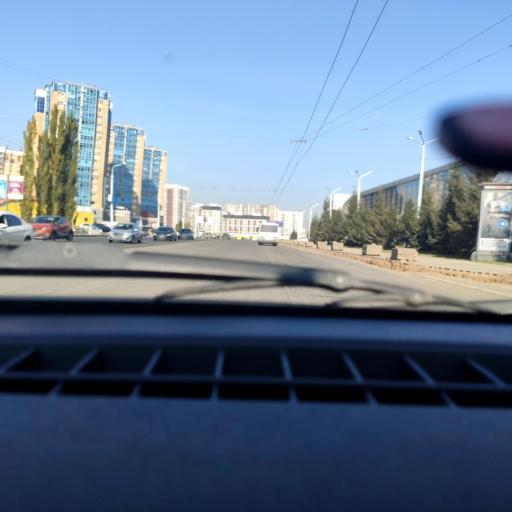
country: RU
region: Bashkortostan
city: Ufa
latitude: 54.7506
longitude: 56.0314
